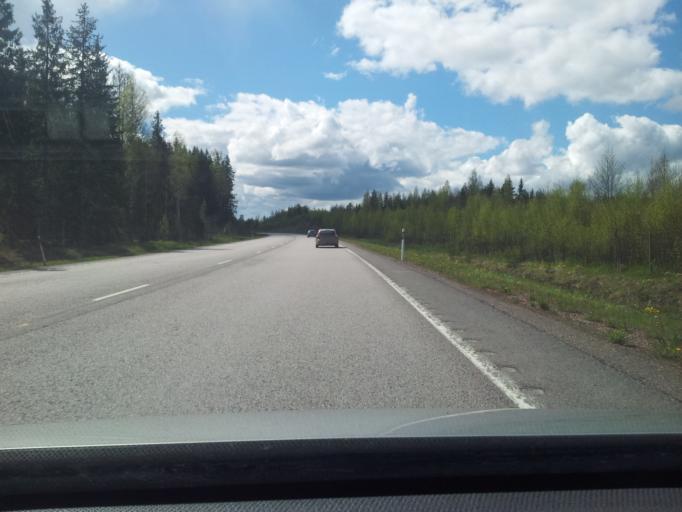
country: FI
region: Uusimaa
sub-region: Loviisa
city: Liljendal
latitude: 60.5243
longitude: 25.9669
